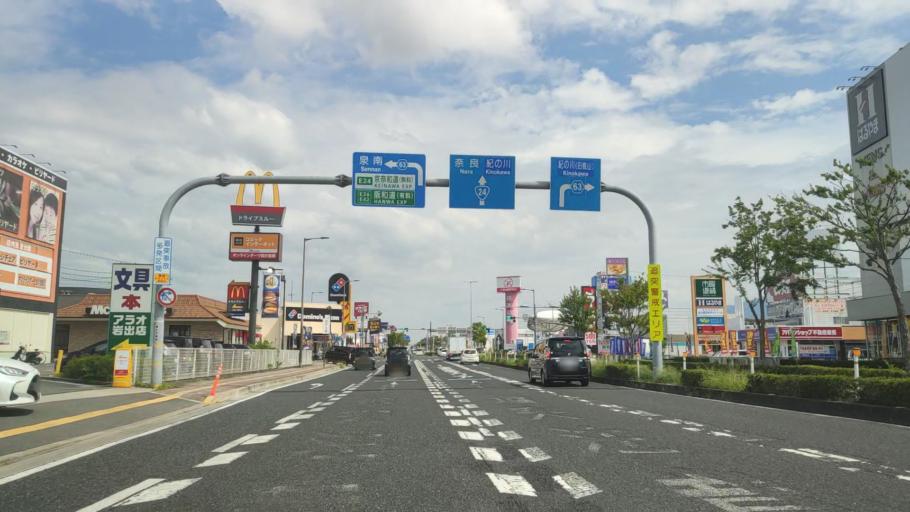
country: JP
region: Wakayama
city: Iwade
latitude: 34.2603
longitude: 135.3118
